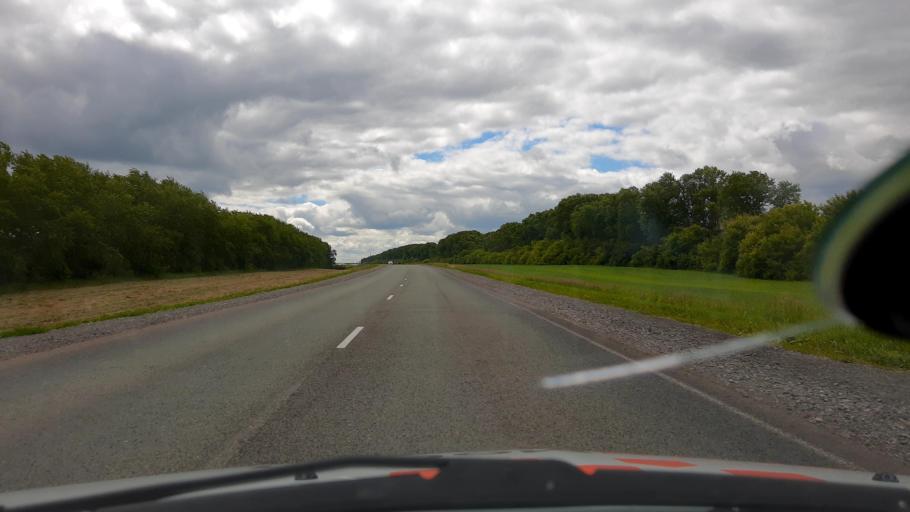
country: RU
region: Bashkortostan
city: Buzdyak
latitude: 54.6680
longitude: 54.5448
